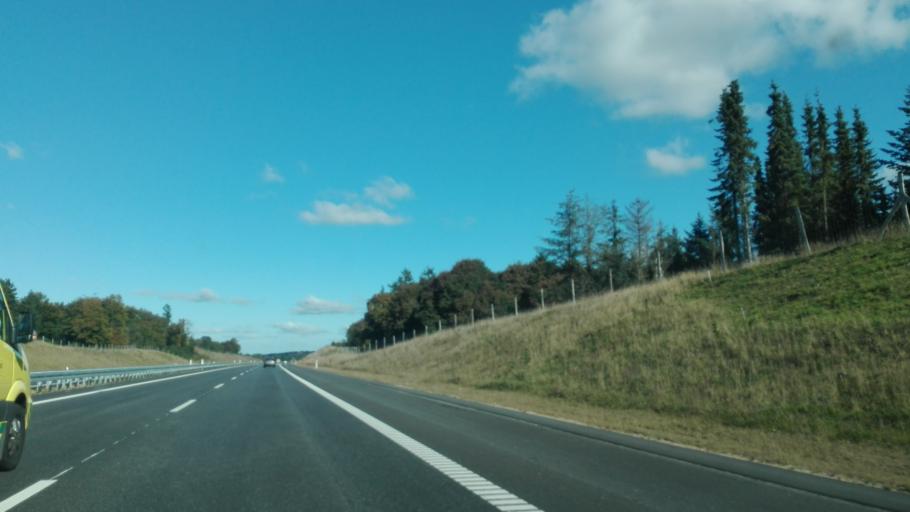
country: DK
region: Central Jutland
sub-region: Silkeborg Kommune
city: Silkeborg
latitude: 56.1734
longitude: 9.4762
